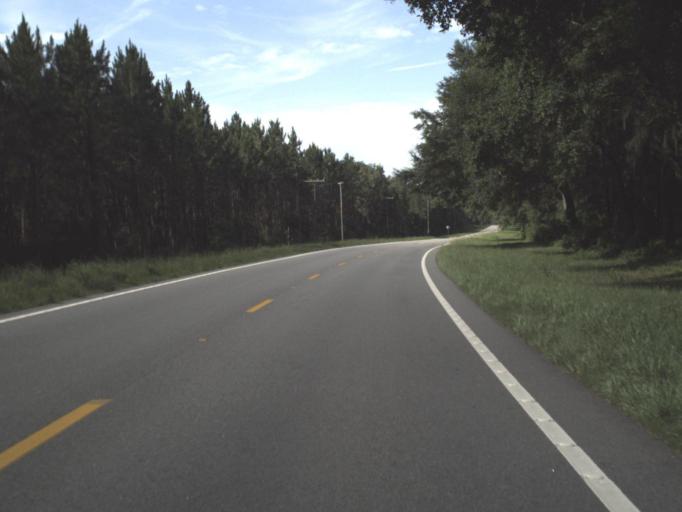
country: US
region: Florida
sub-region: Madison County
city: Madison
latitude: 30.5761
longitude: -83.3567
